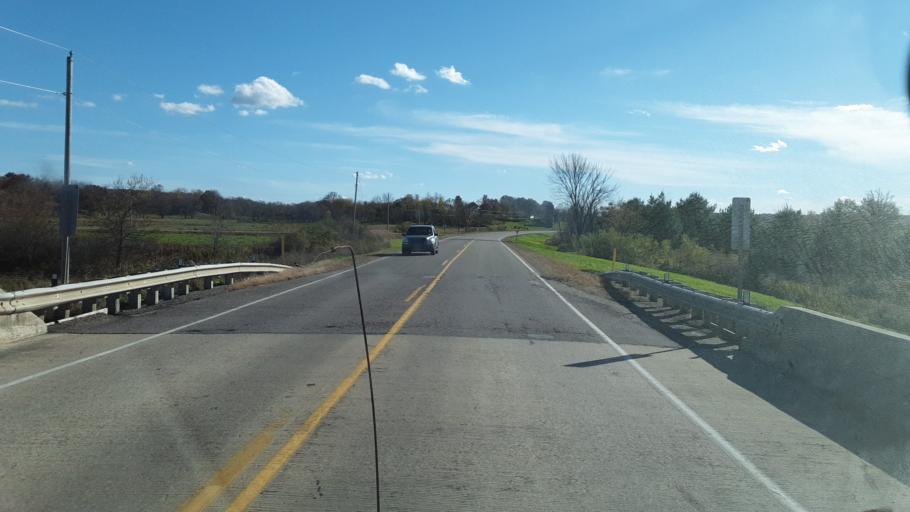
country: US
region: Wisconsin
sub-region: Sauk County
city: Reedsburg
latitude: 43.5639
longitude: -90.1331
